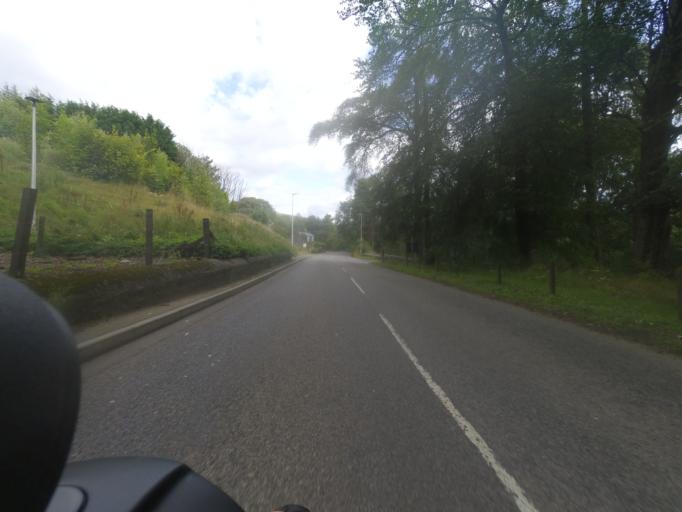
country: GB
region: Scotland
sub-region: Moray
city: Dufftown
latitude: 57.4440
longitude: -3.1201
